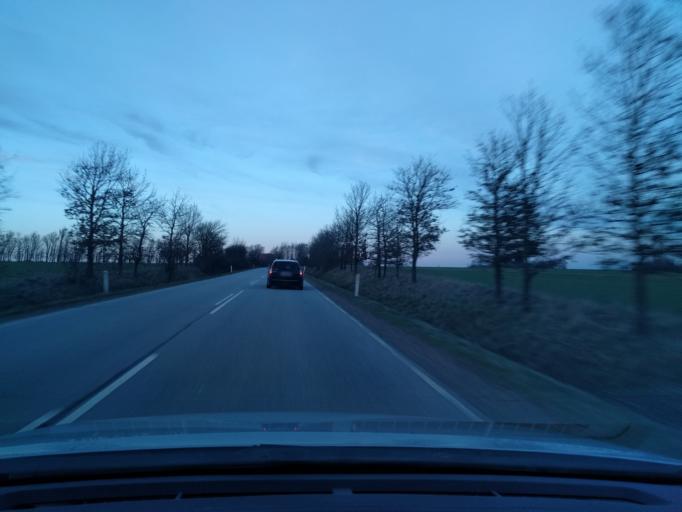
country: DK
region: South Denmark
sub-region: Vejen Kommune
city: Rodding
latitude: 55.3221
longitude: 9.1448
